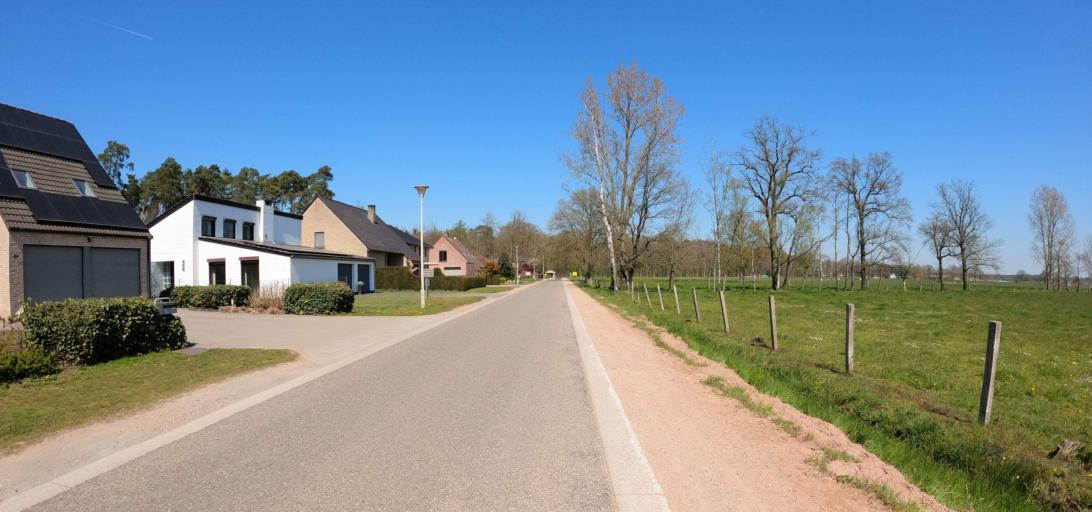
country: BE
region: Flanders
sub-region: Provincie Antwerpen
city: Oostmalle
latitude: 51.3055
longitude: 4.7529
